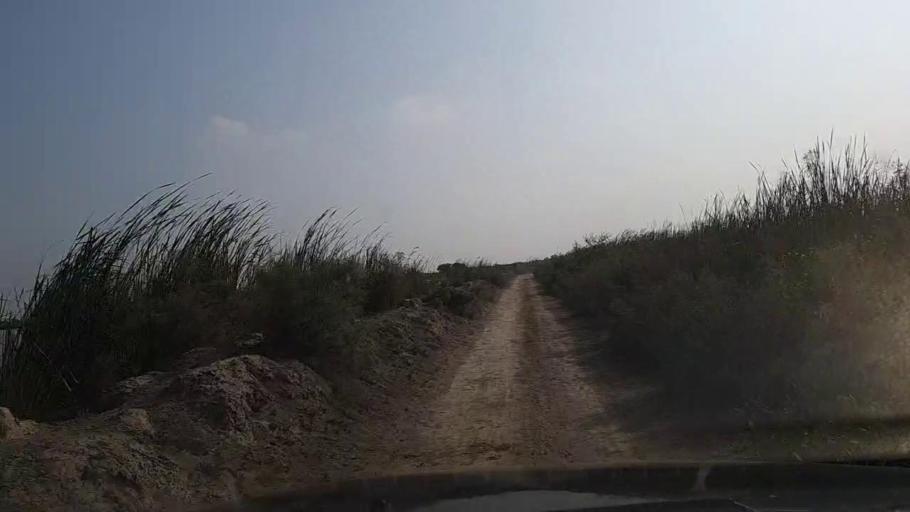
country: PK
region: Sindh
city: Mirpur Batoro
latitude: 24.6471
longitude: 68.2826
